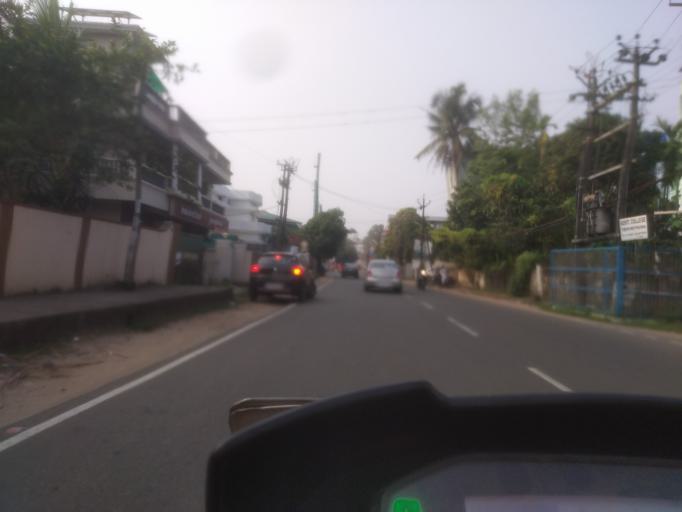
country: IN
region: Kerala
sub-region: Alappuzha
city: Arukutti
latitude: 9.9405
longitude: 76.3472
